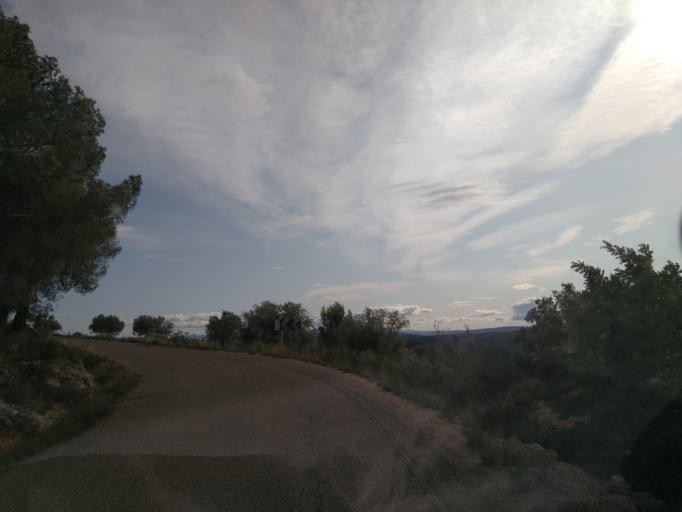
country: ES
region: Valencia
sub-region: Provincia de Valencia
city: Sumacarcer
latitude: 39.1463
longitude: -0.6459
